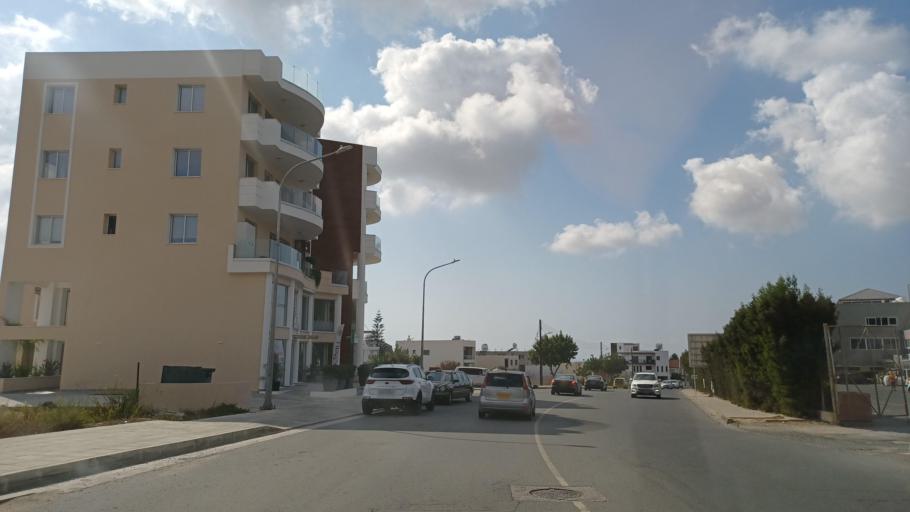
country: CY
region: Pafos
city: Mesogi
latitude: 34.7985
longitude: 32.4487
